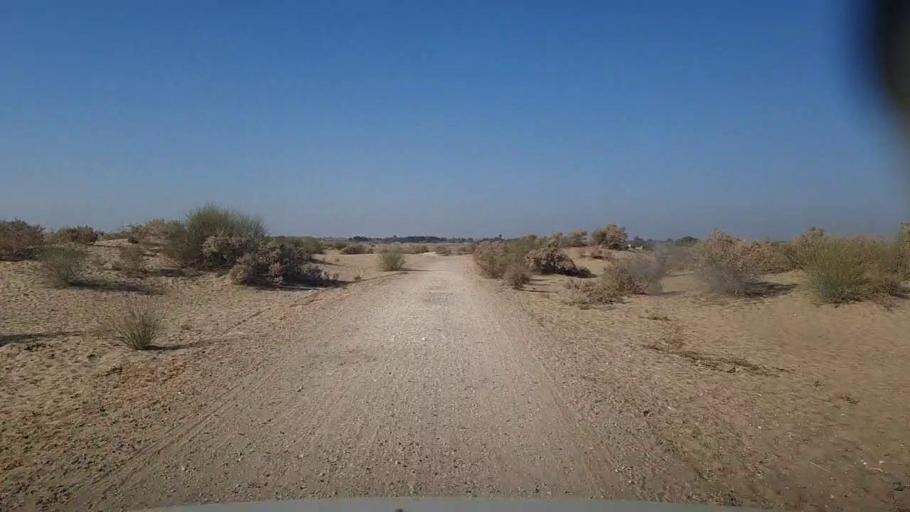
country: PK
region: Sindh
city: Khairpur
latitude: 27.9616
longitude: 69.8119
